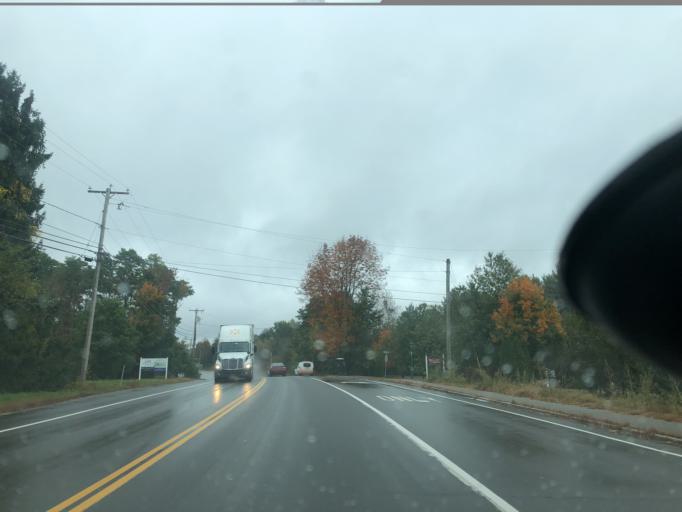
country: US
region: New Hampshire
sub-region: Strafford County
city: Dover
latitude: 43.1808
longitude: -70.8938
